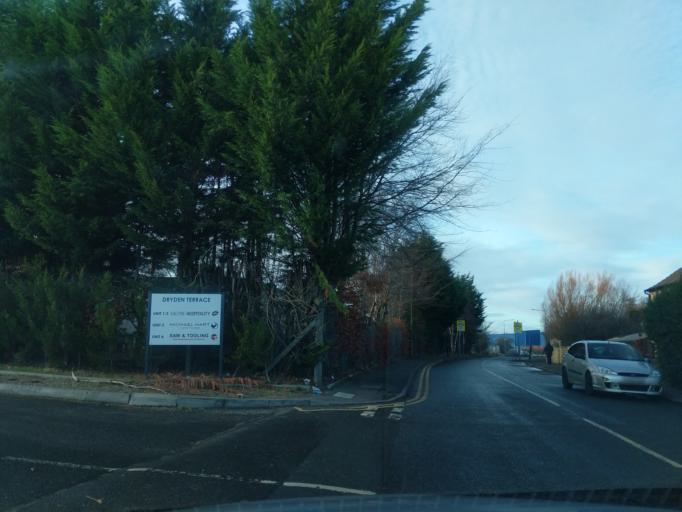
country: GB
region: Scotland
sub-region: Midlothian
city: Loanhead
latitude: 55.8773
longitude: -3.1649
